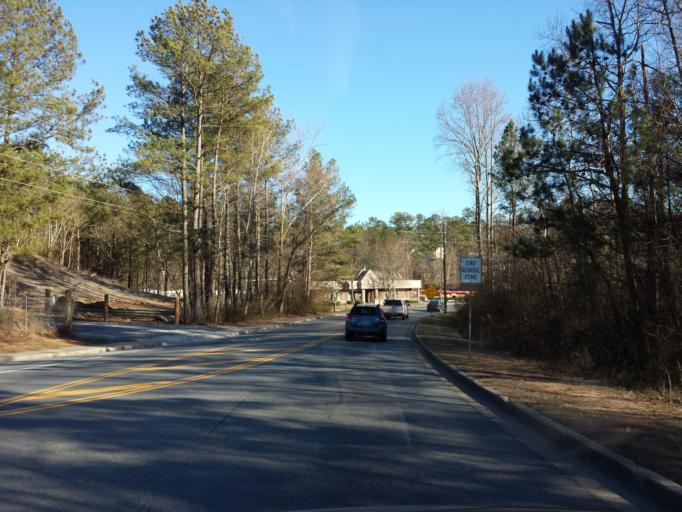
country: US
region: Georgia
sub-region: Cobb County
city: Marietta
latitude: 33.9703
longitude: -84.5154
